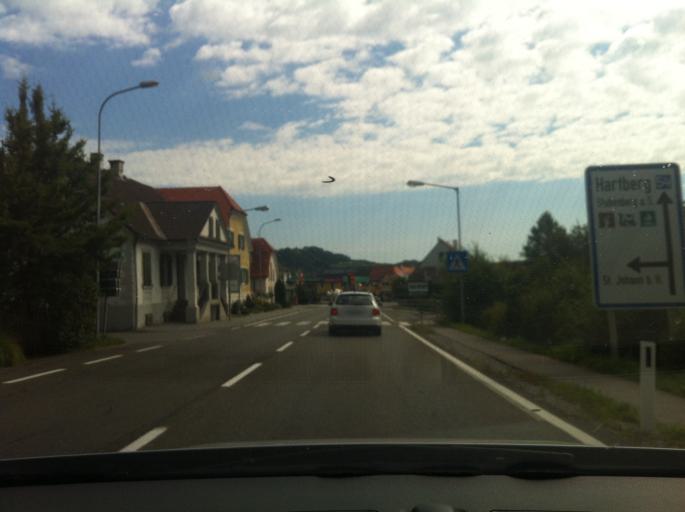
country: AT
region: Styria
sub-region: Politischer Bezirk Hartberg-Fuerstenfeld
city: Kaibing
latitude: 47.1931
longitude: 15.8258
